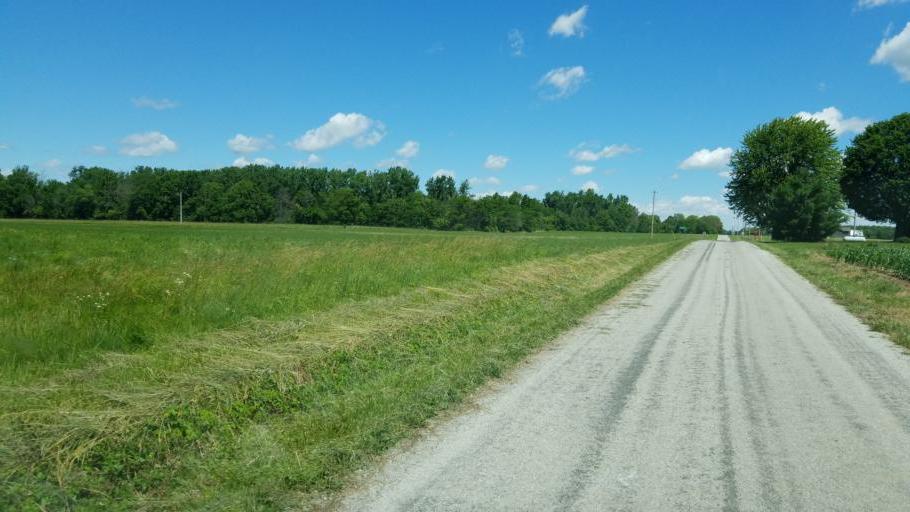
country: US
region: Ohio
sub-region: Crawford County
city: Bucyrus
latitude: 40.6735
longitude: -82.9389
